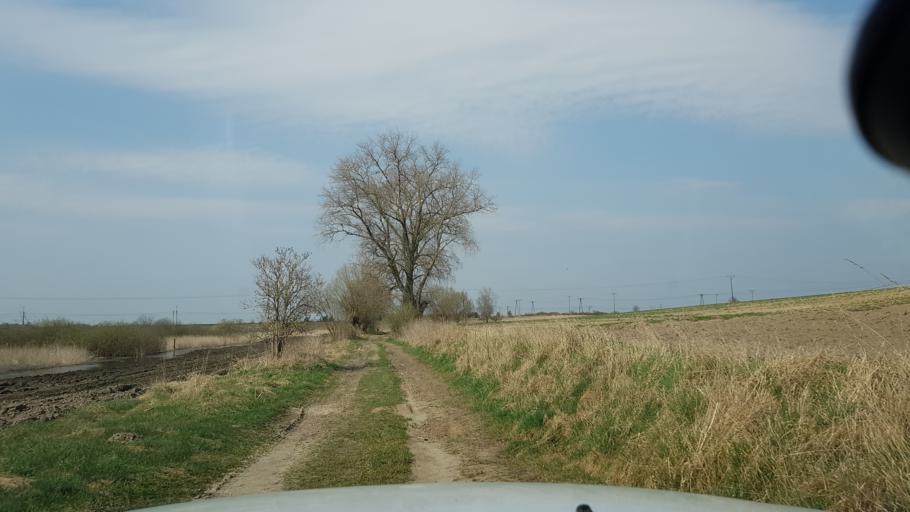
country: PL
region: West Pomeranian Voivodeship
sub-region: Powiat stargardzki
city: Stargard Szczecinski
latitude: 53.3298
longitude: 15.0820
